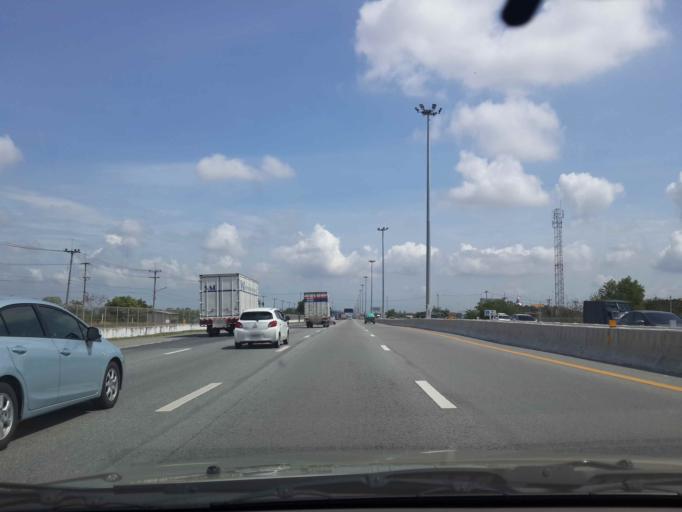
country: TH
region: Chachoengsao
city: Bang Pakong
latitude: 13.5224
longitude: 101.0230
